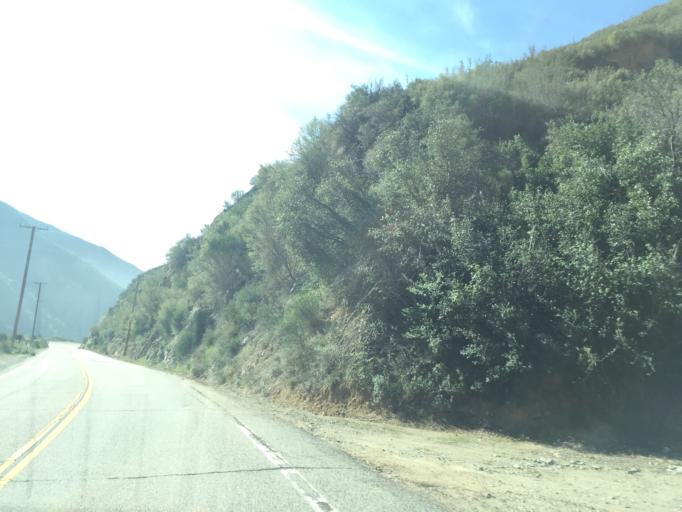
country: US
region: California
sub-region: San Bernardino County
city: San Antonio Heights
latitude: 34.1910
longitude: -117.6782
